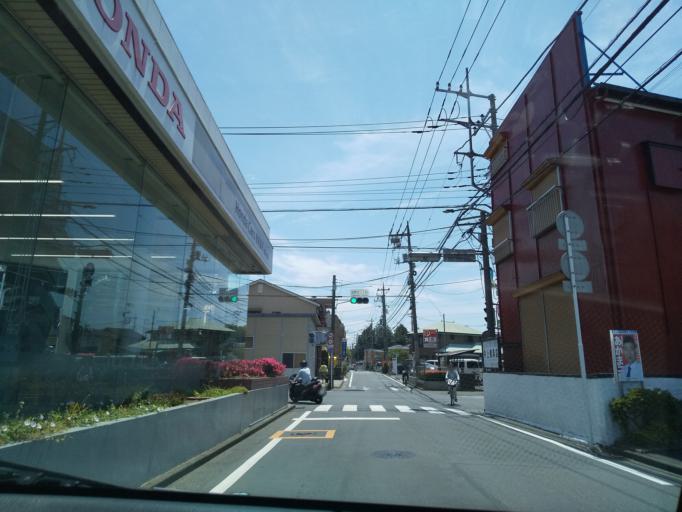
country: JP
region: Tokyo
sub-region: Machida-shi
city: Machida
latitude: 35.5566
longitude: 139.3989
